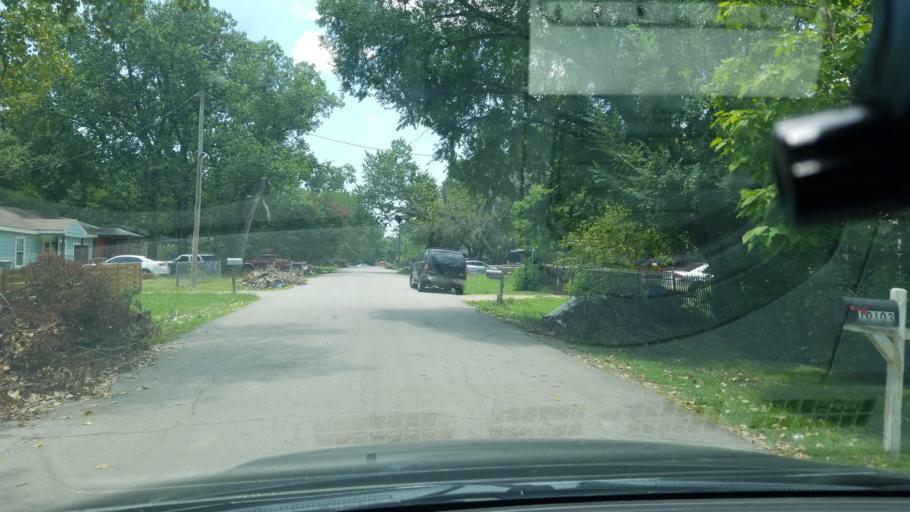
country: US
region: Texas
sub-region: Dallas County
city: Balch Springs
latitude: 32.7159
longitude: -96.6499
